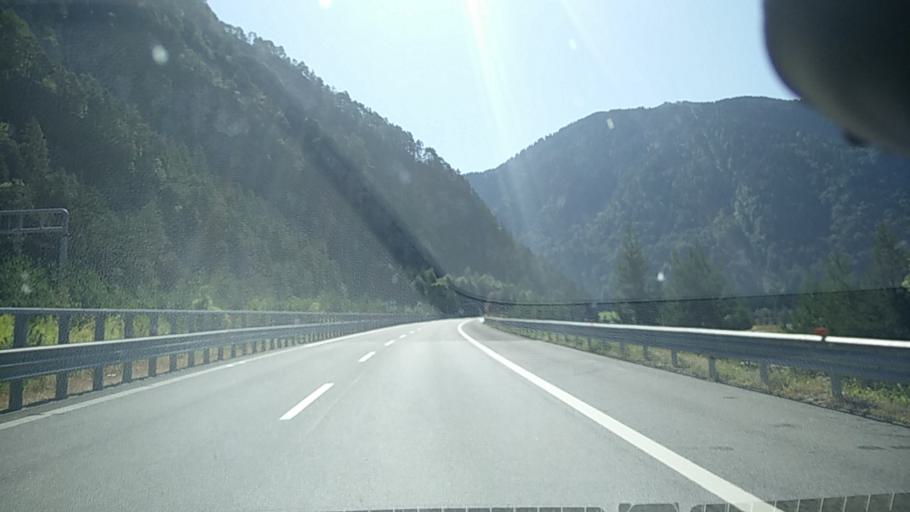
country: IT
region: Friuli Venezia Giulia
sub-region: Provincia di Udine
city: Malborghetto
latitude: 46.5055
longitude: 13.4921
